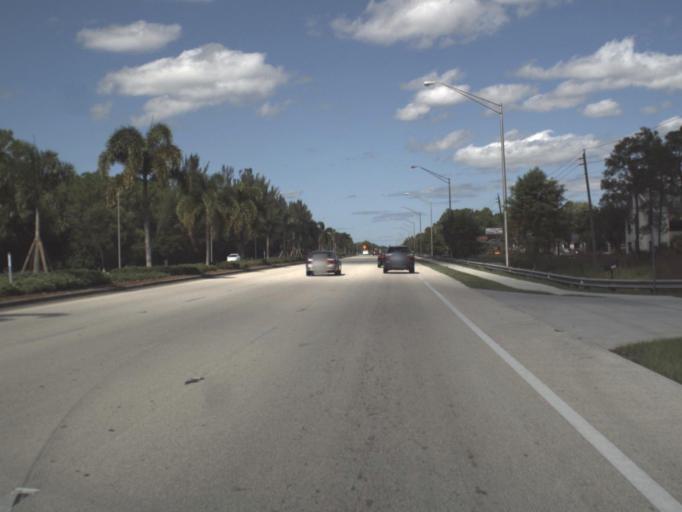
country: US
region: Florida
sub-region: Collier County
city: Naples Manor
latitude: 26.0828
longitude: -81.7256
